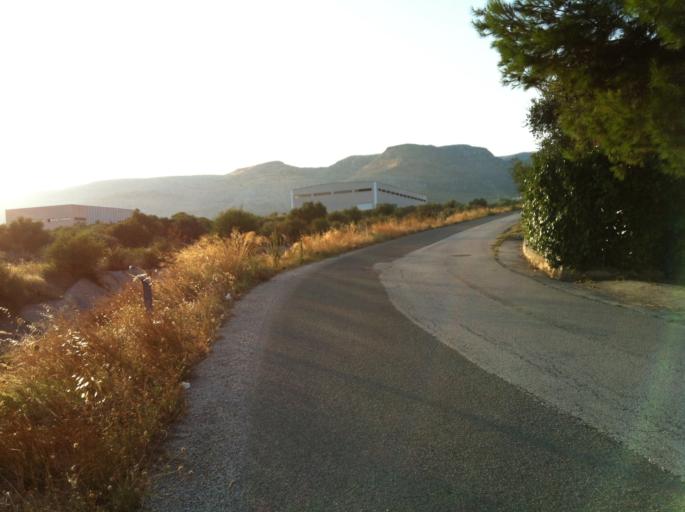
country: IT
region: Apulia
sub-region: Provincia di Foggia
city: Manfredonia
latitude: 41.6527
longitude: 15.9532
